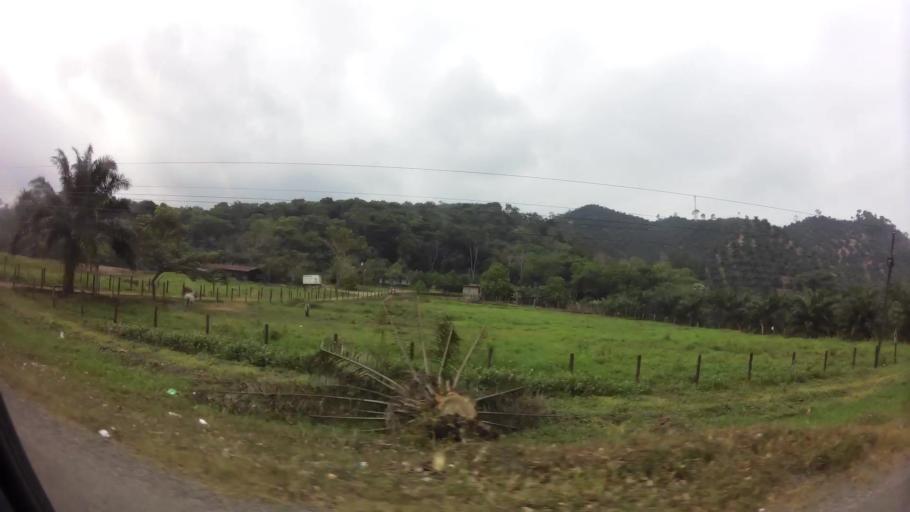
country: HN
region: Yoro
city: Guaimitas
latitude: 15.4942
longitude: -87.7337
